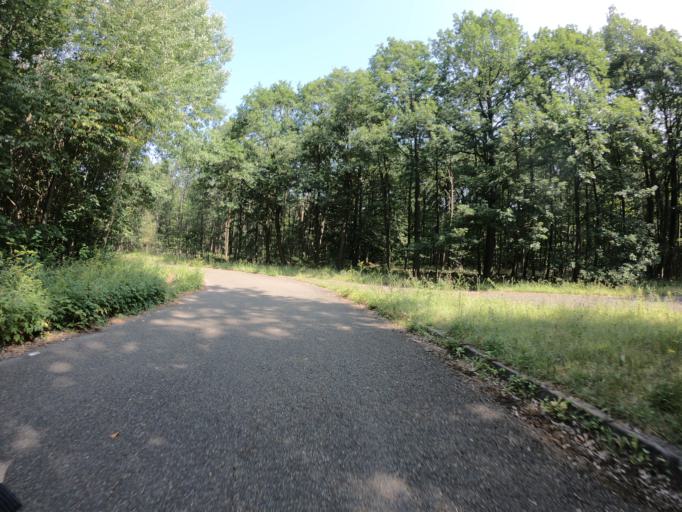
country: FR
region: Ile-de-France
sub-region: Departement de l'Essonne
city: Igny
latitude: 48.7532
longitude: 2.2360
